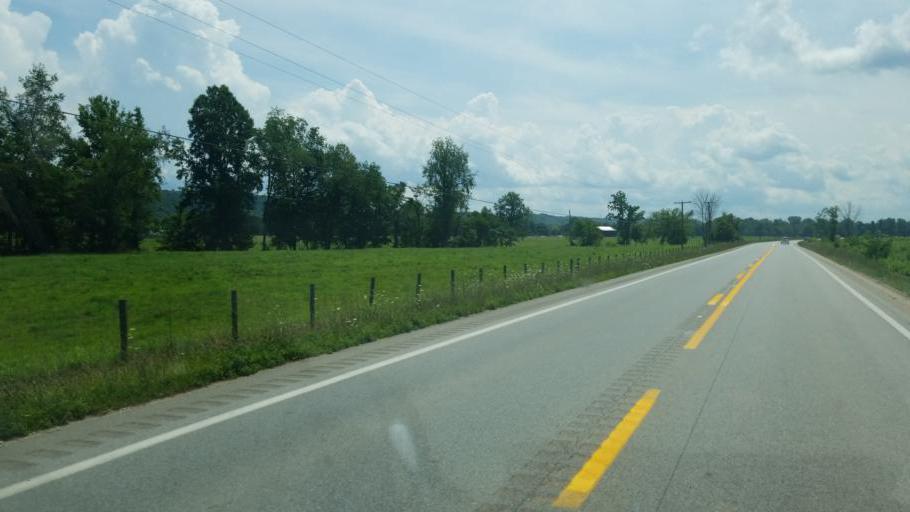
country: US
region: West Virginia
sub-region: Putnam County
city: Buffalo
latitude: 38.6341
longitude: -81.9780
